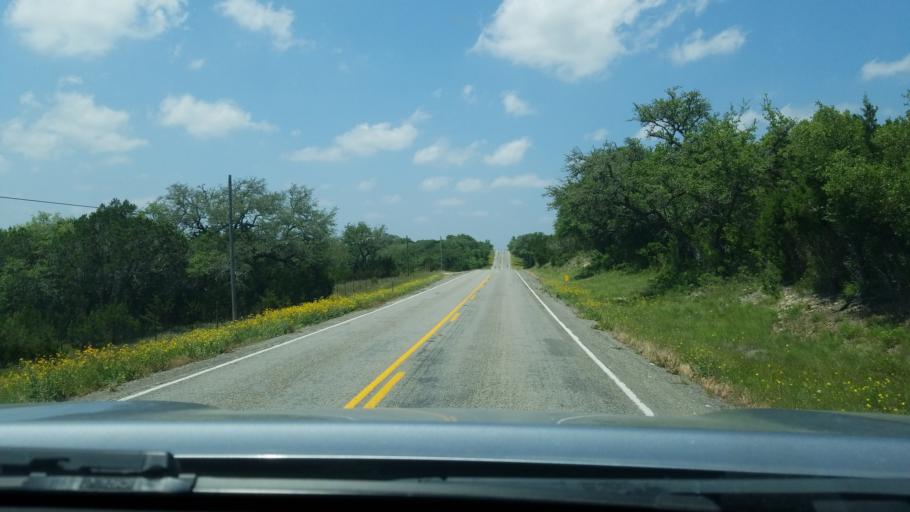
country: US
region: Texas
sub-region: Hays County
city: Woodcreek
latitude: 30.0606
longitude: -98.2100
